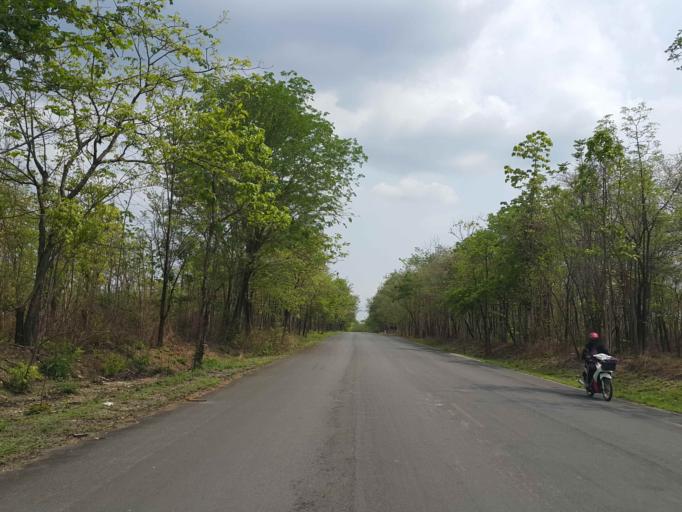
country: TH
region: Lampang
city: Thoen
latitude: 17.4493
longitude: 99.3716
